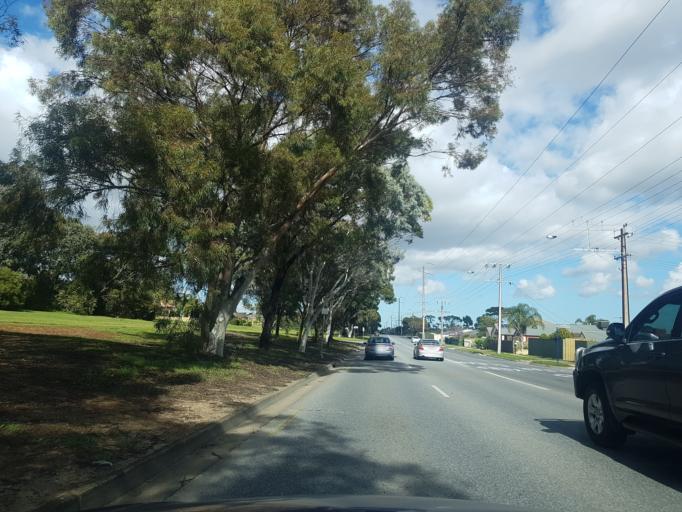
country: AU
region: South Australia
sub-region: Salisbury
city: Salisbury
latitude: -34.7900
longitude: 138.6643
